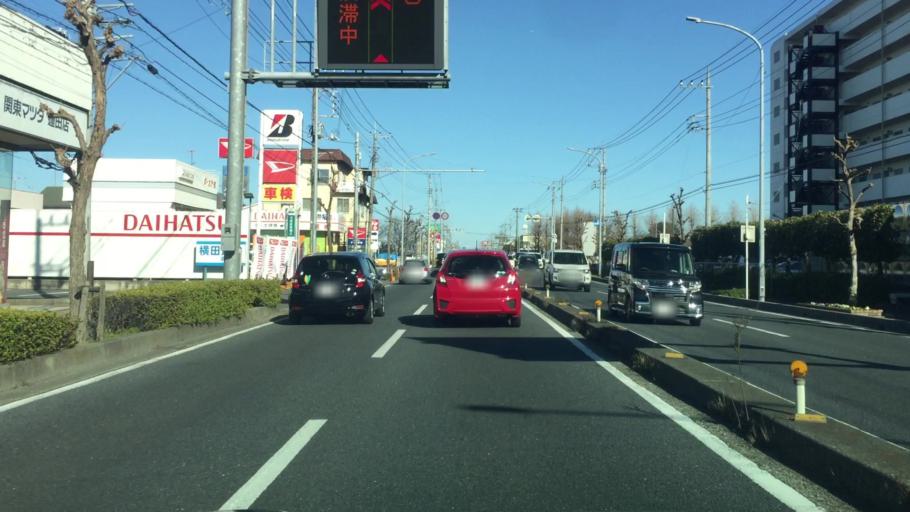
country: JP
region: Saitama
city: Hasuda
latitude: 35.9813
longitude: 139.6425
